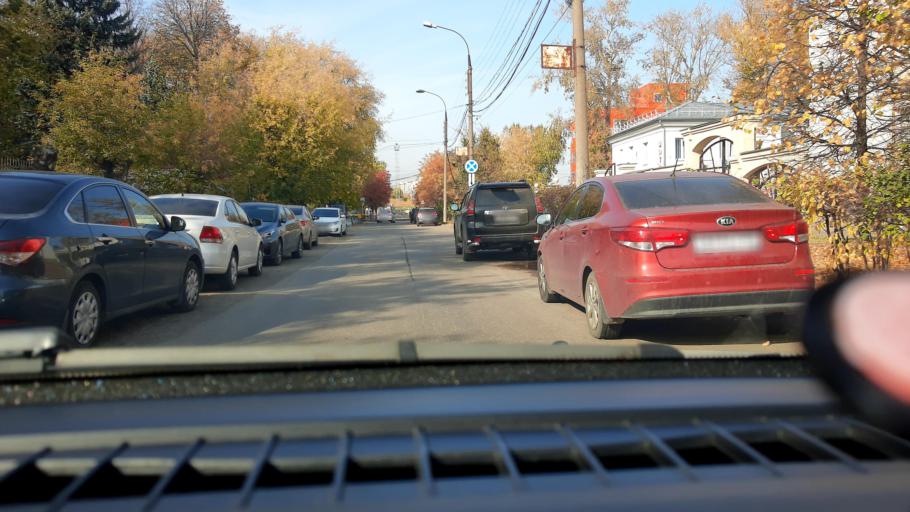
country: RU
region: Nizjnij Novgorod
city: Nizhniy Novgorod
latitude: 56.2536
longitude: 43.8892
